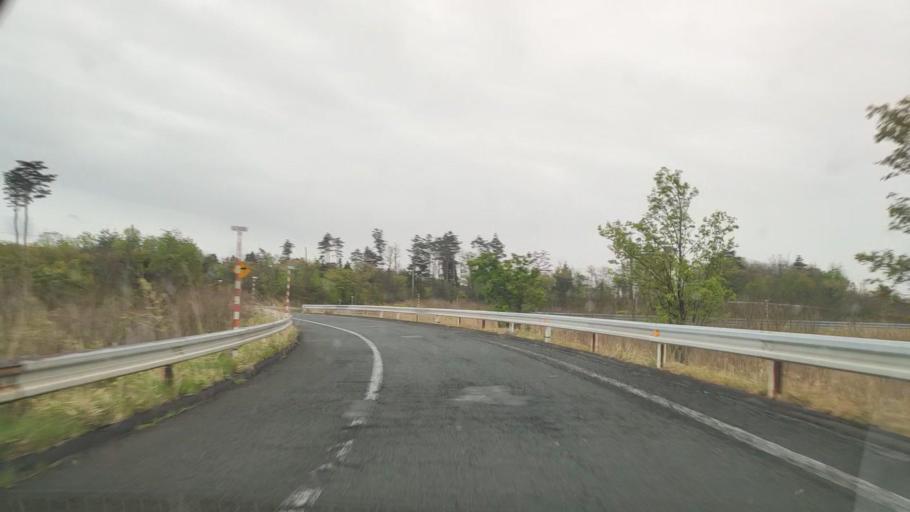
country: JP
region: Akita
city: Noshiromachi
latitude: 40.1198
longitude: 140.0120
